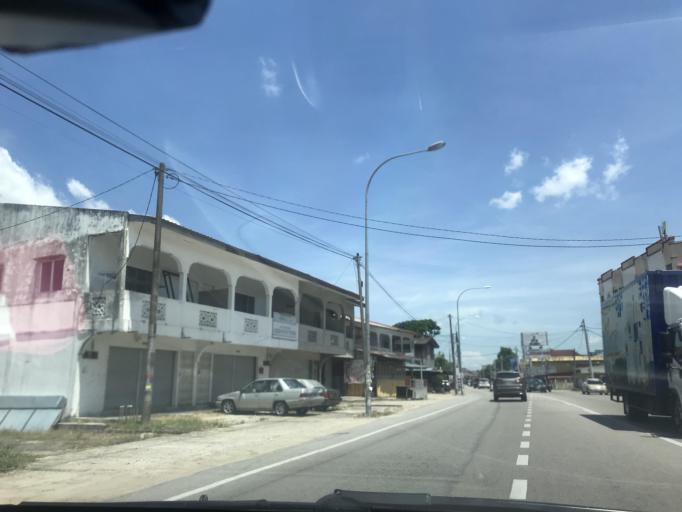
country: MY
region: Kelantan
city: Kota Bharu
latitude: 6.1248
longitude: 102.2627
